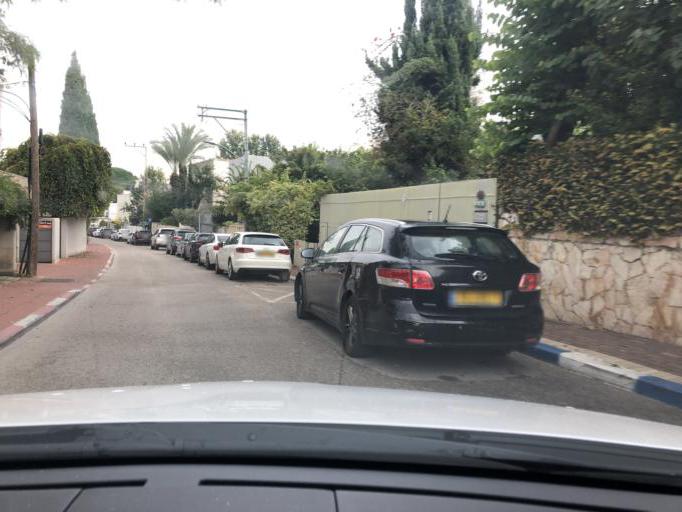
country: IL
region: Tel Aviv
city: Giv`atayim
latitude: 32.0571
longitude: 34.8204
